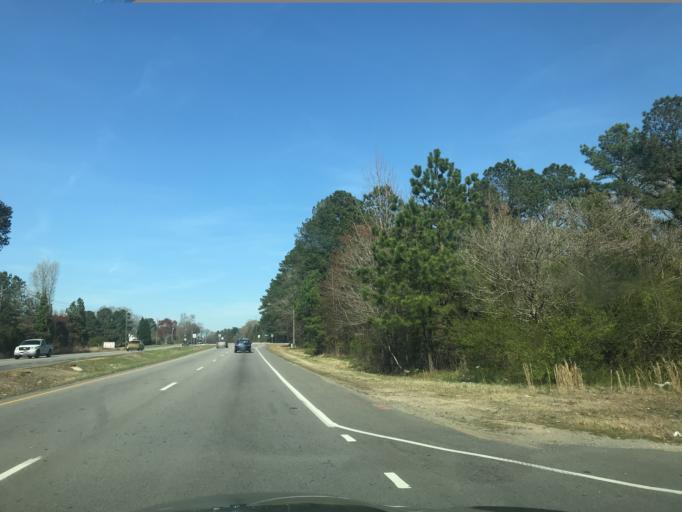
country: US
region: North Carolina
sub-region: Wake County
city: Garner
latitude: 35.6675
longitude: -78.6964
